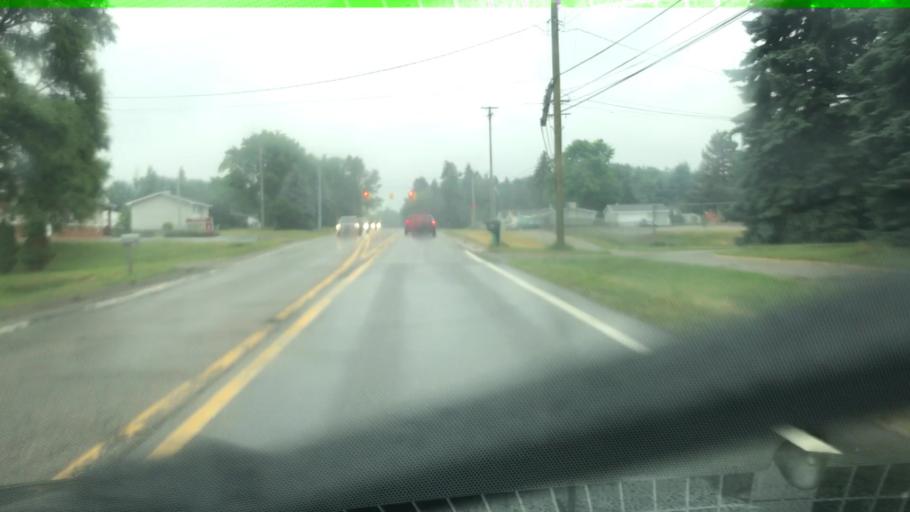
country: US
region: Michigan
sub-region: Oakland County
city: Auburn Hills
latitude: 42.7286
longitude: -83.2877
